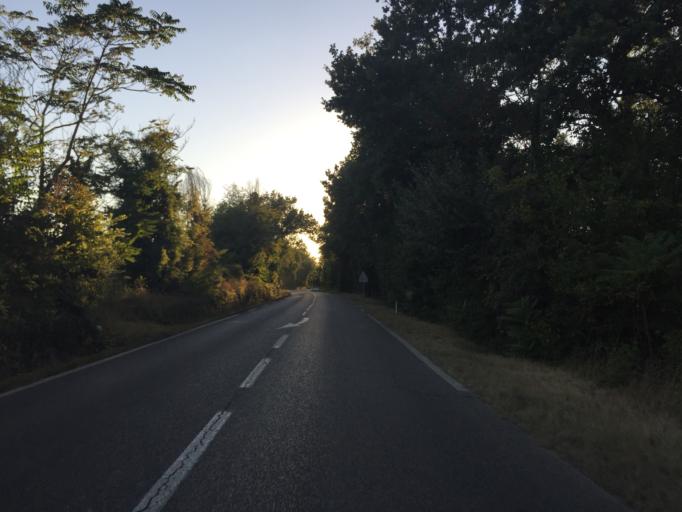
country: FR
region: Provence-Alpes-Cote d'Azur
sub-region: Departement du Vaucluse
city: Saignon
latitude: 43.8800
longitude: 5.4412
